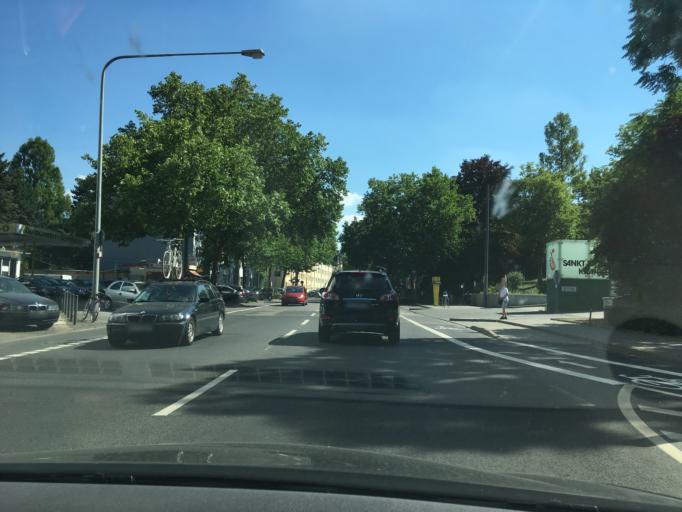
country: DE
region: Hesse
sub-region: Regierungsbezirk Darmstadt
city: Frankfurt am Main
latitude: 50.1362
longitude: 8.7123
